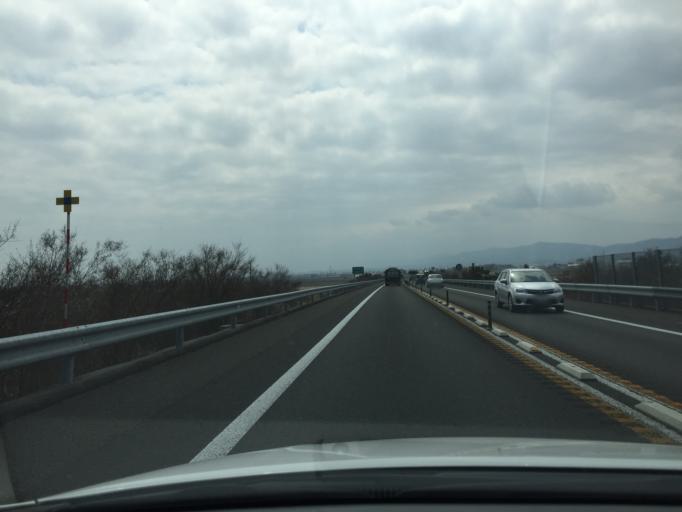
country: JP
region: Miyagi
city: Watari
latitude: 38.0248
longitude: 140.8896
